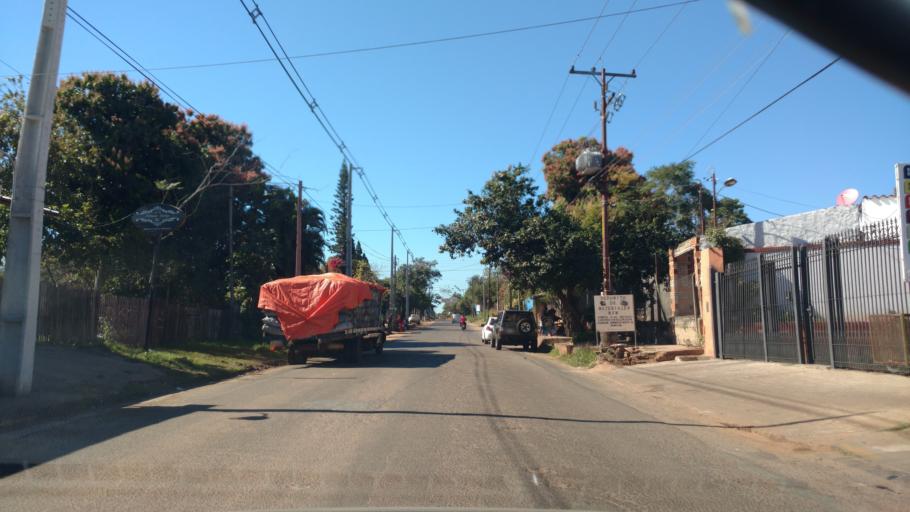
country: PY
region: Central
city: Itaugua
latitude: -25.3996
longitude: -57.3429
